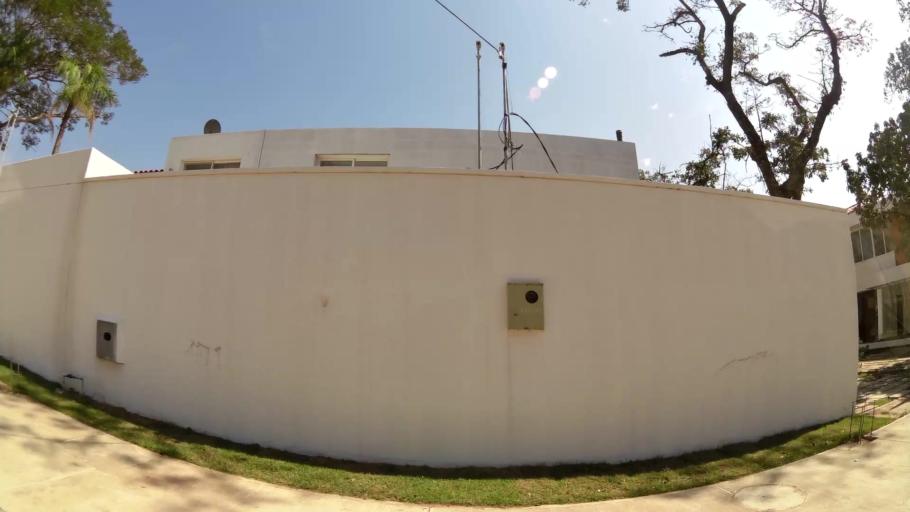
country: BO
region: Santa Cruz
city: Santa Cruz de la Sierra
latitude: -17.7469
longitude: -63.1816
